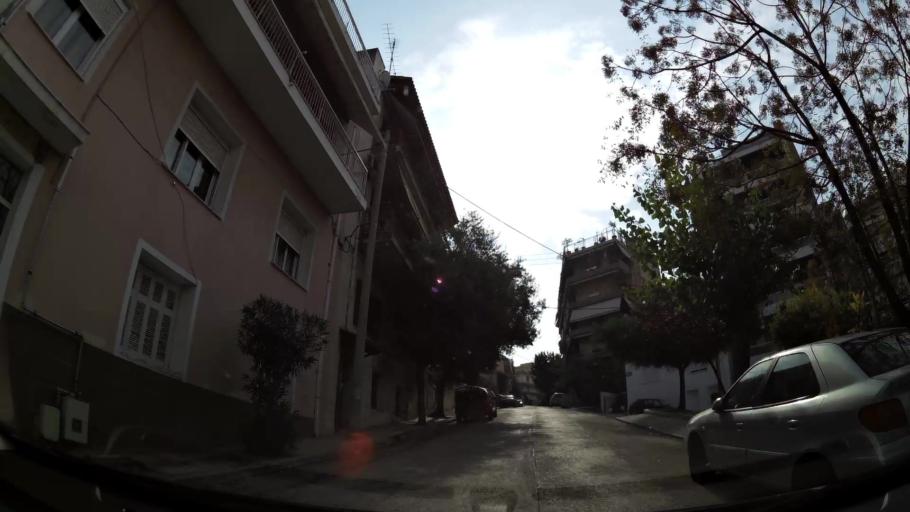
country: GR
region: Attica
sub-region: Nomarchia Athinas
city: Galatsi
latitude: 38.0152
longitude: 23.7585
